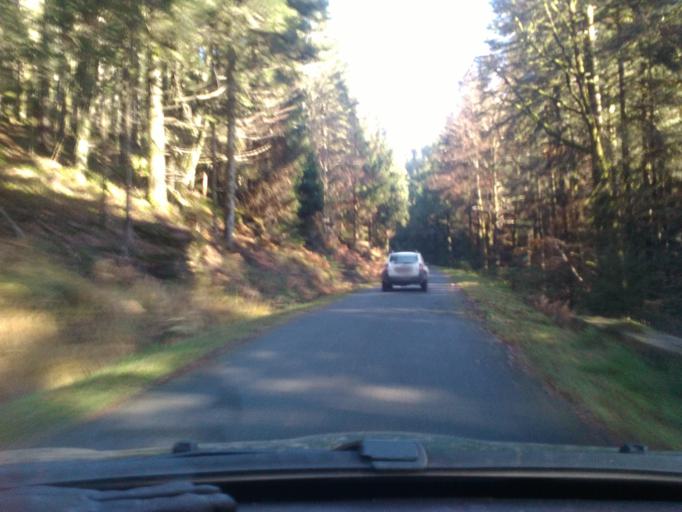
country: FR
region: Lorraine
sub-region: Departement des Vosges
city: Senones
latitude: 48.4619
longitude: 7.0632
